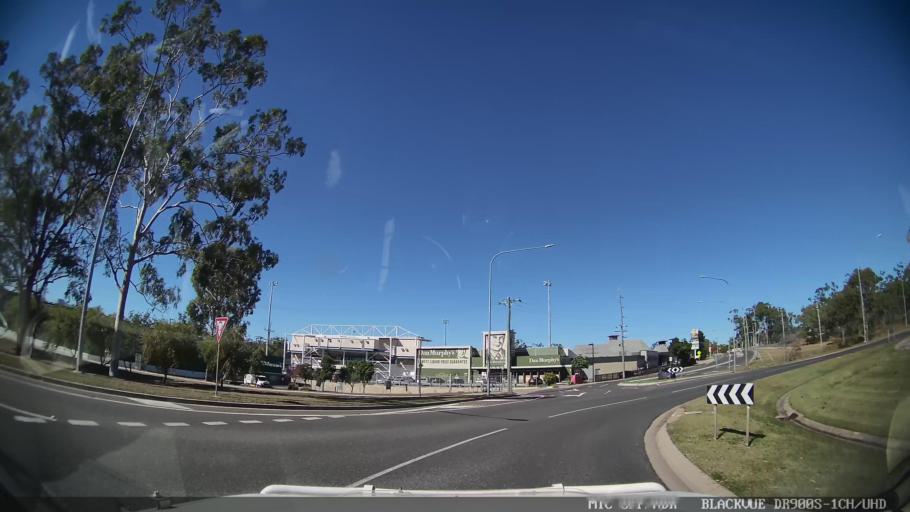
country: AU
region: Queensland
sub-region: Gladstone
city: Gladstone
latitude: -23.8770
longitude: 151.2236
